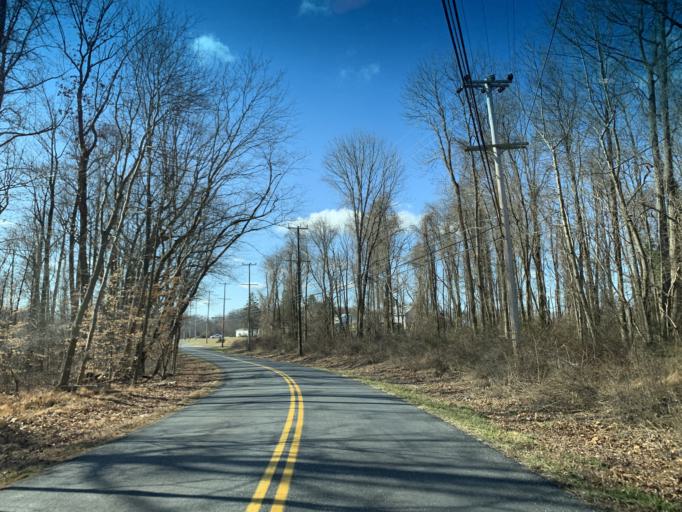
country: US
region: Maryland
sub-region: Harford County
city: Riverside
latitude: 39.5169
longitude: -76.2320
